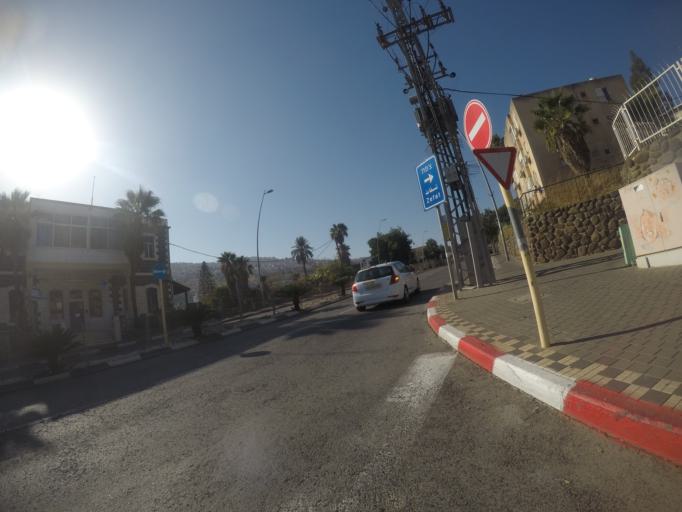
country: IL
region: Northern District
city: Tiberias
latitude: 32.7912
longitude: 35.5378
